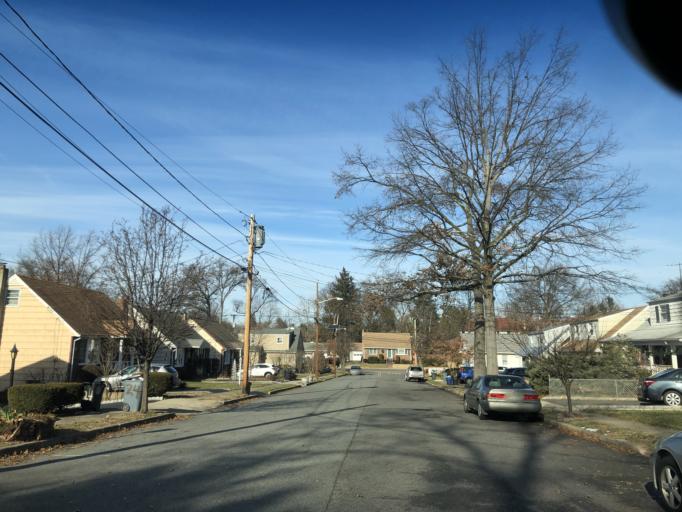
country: US
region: New Jersey
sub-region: Bergen County
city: Fair Lawn
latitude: 40.9221
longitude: -74.1280
